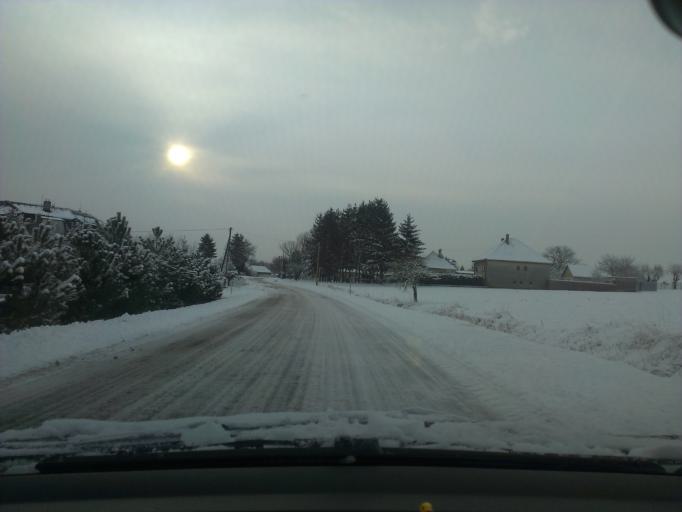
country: SK
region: Trnavsky
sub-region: Okres Trnava
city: Piestany
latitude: 48.5282
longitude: 17.9618
